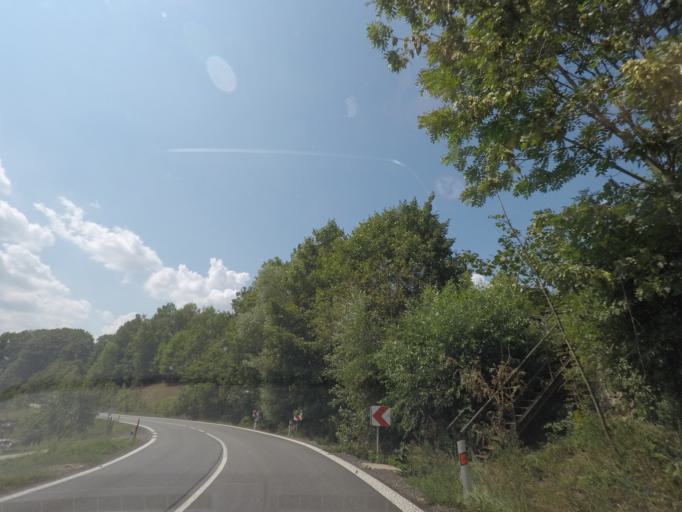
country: CZ
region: Kralovehradecky
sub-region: Okres Trutnov
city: Hostinne
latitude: 50.5229
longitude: 15.7617
